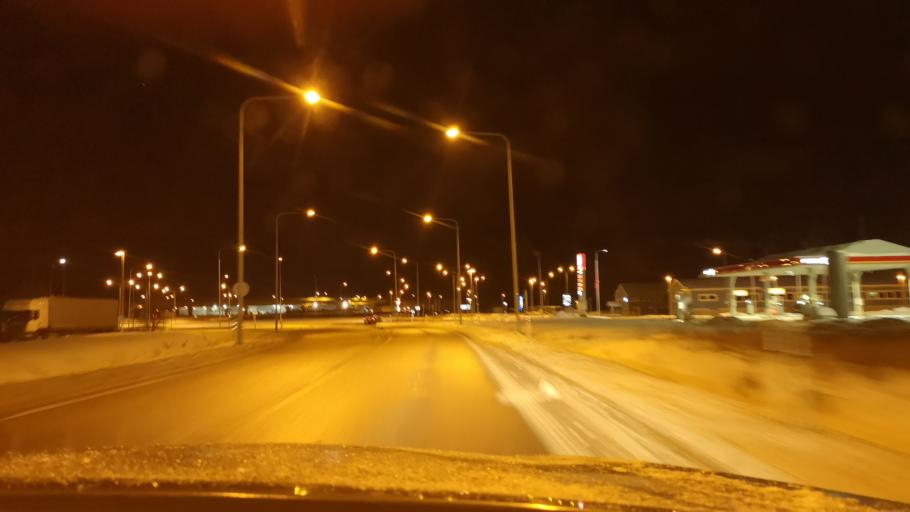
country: EE
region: Harju
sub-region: Joelaehtme vald
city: Loo
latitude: 59.4497
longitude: 24.9220
